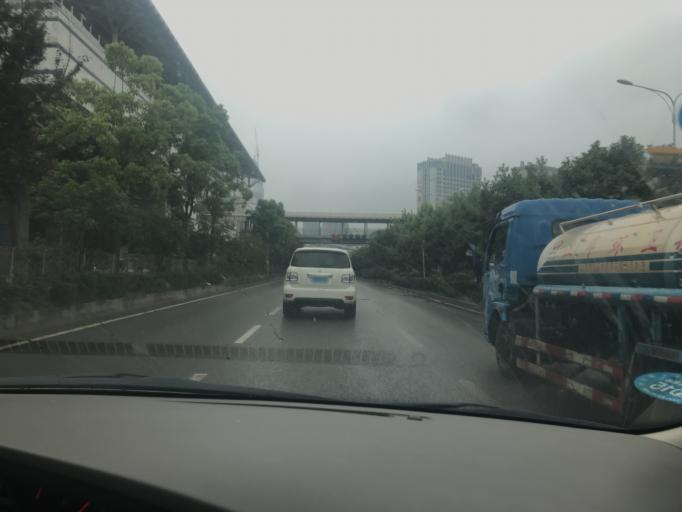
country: CN
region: Hubei
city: Jiang'an
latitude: 30.6211
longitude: 114.3088
